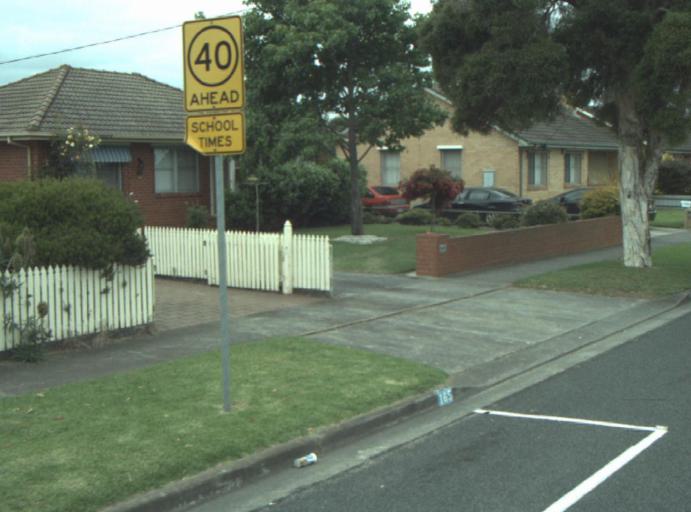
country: AU
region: Victoria
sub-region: Greater Geelong
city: Breakwater
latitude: -38.1726
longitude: 144.3781
